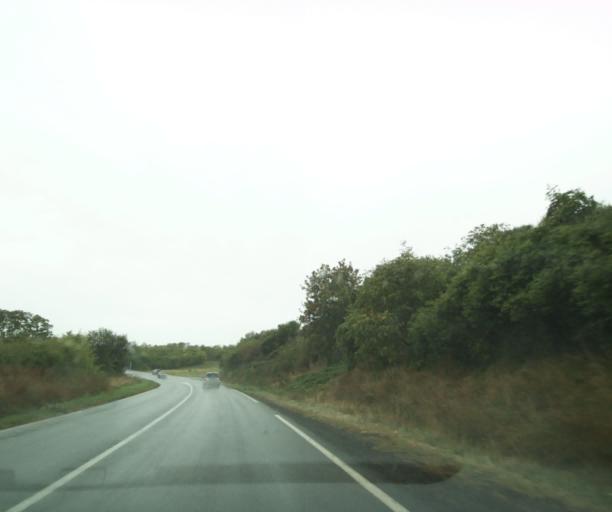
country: FR
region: Auvergne
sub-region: Departement du Puy-de-Dome
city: Cebazat
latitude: 45.8441
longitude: 3.1068
